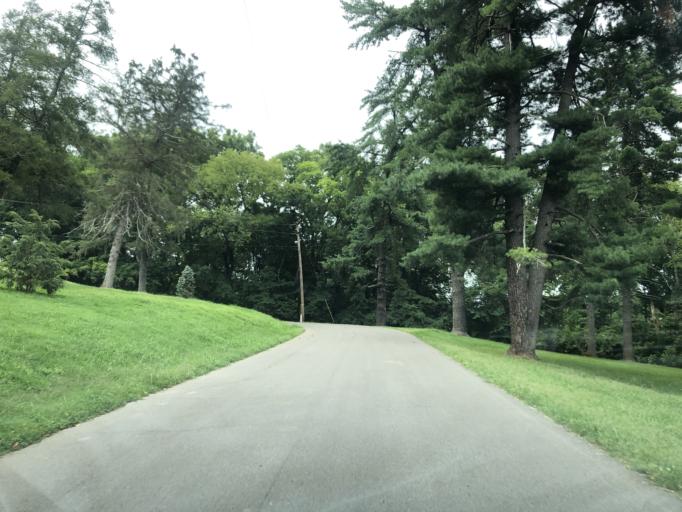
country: US
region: Tennessee
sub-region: Davidson County
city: Nashville
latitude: 36.1675
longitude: -86.7328
